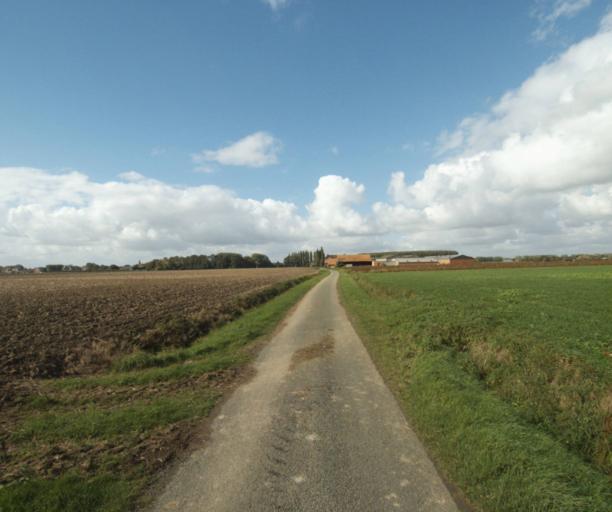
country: FR
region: Nord-Pas-de-Calais
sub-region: Departement du Nord
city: Frelinghien
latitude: 50.7149
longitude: 2.9474
